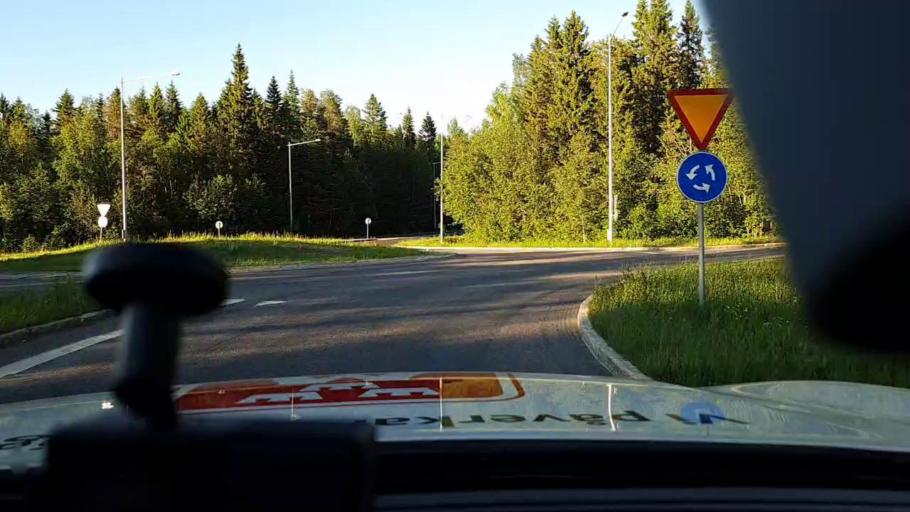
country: SE
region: Norrbotten
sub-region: Lulea Kommun
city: Lulea
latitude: 65.6085
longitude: 22.1827
